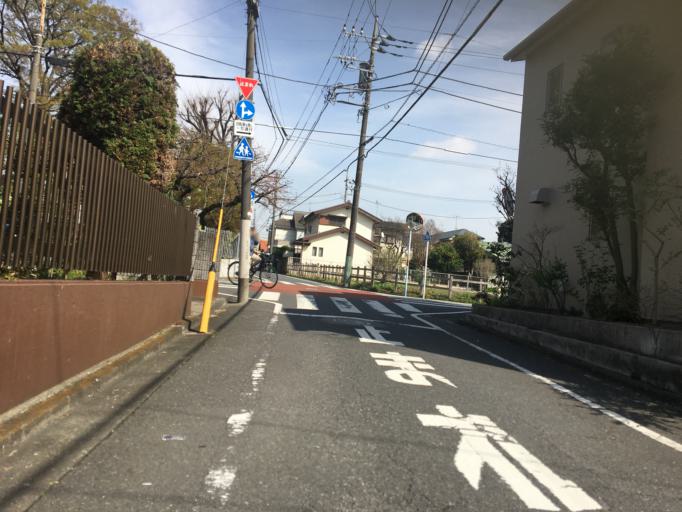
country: JP
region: Tokyo
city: Musashino
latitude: 35.7216
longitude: 139.6168
